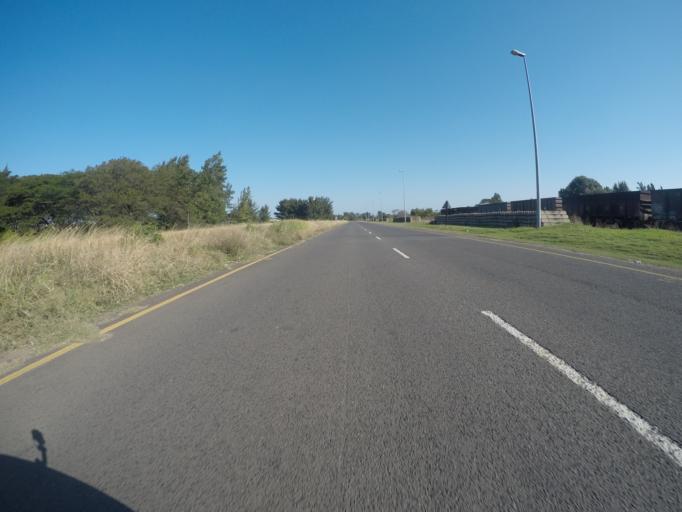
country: ZA
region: KwaZulu-Natal
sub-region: uThungulu District Municipality
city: Richards Bay
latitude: -28.7894
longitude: 32.0788
